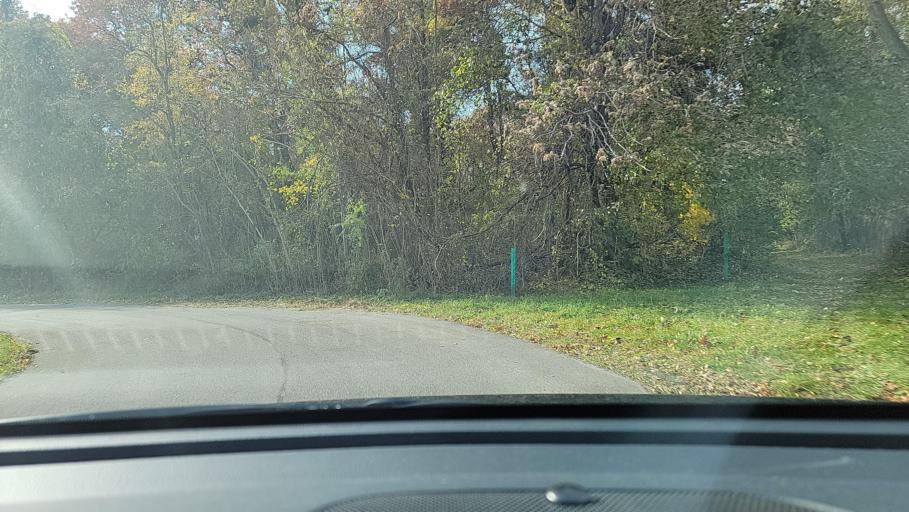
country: US
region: Indiana
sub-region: Lake County
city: Lake Station
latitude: 41.5852
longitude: -87.2157
